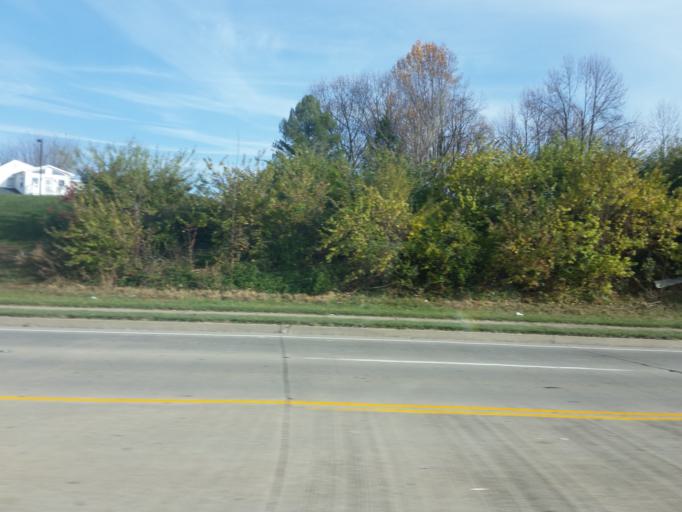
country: US
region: Kentucky
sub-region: Campbell County
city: Alexandria
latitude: 38.9632
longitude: -84.3928
